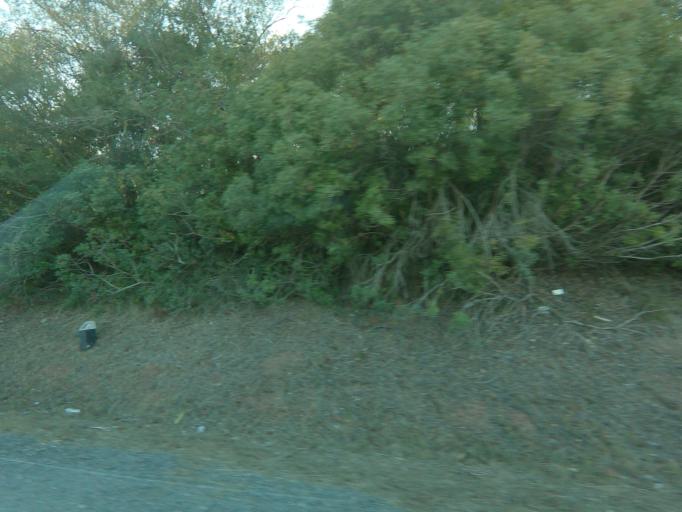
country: PT
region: Setubal
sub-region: Palmela
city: Quinta do Anjo
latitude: 38.5108
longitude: -8.9718
